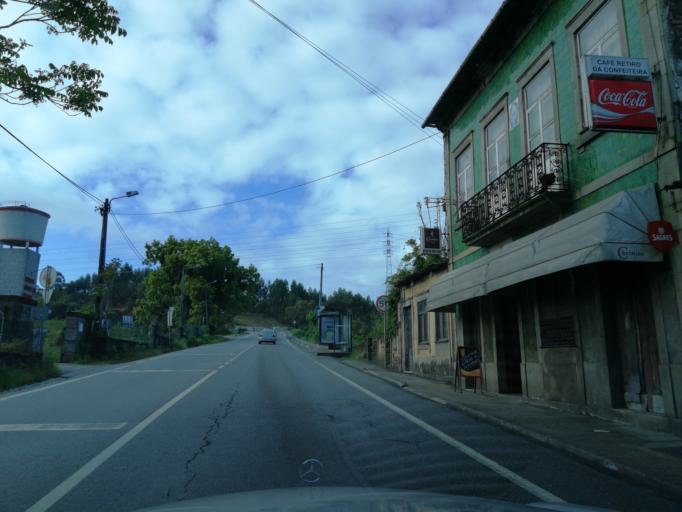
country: PT
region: Braga
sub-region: Braga
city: Braga
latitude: 41.5713
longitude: -8.4231
